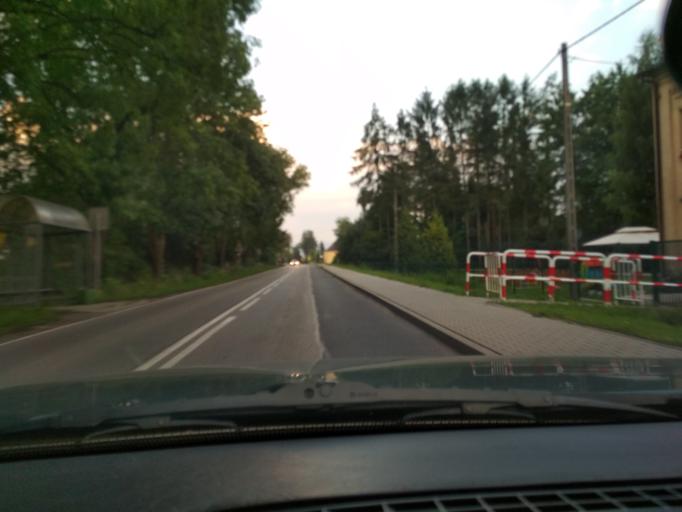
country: PL
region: Silesian Voivodeship
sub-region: Powiat cieszynski
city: Zablocie
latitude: 49.9058
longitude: 18.7763
